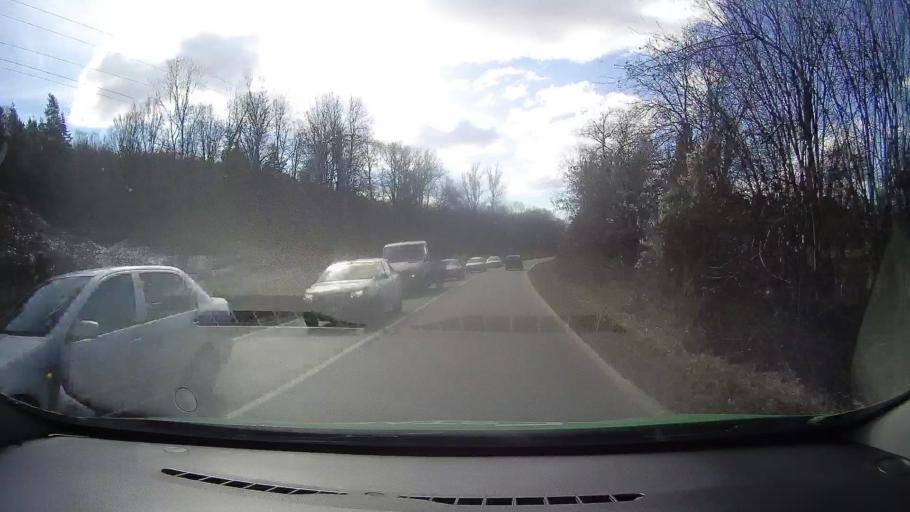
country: RO
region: Dambovita
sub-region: Comuna Vulcana-Pandele
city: Gura Vulcanei
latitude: 45.0163
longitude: 25.4094
